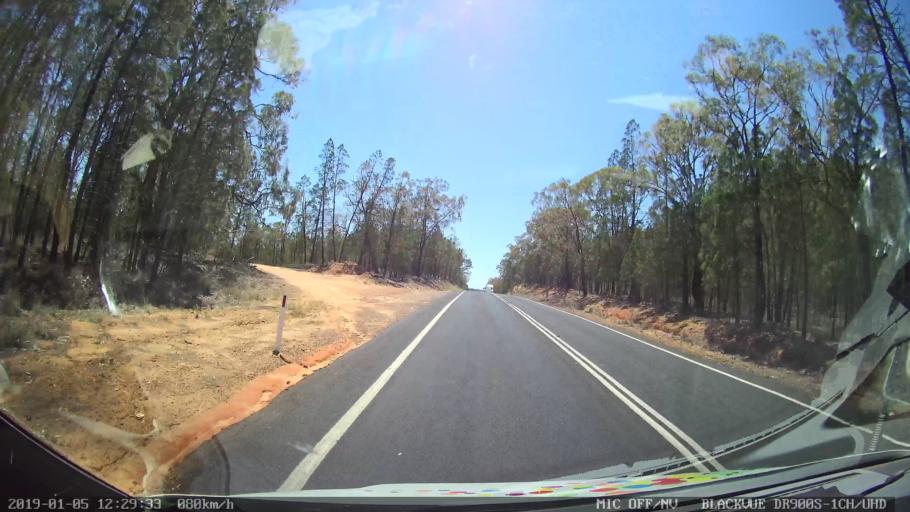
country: AU
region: New South Wales
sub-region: Warrumbungle Shire
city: Coonabarabran
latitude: -31.2325
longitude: 149.3386
